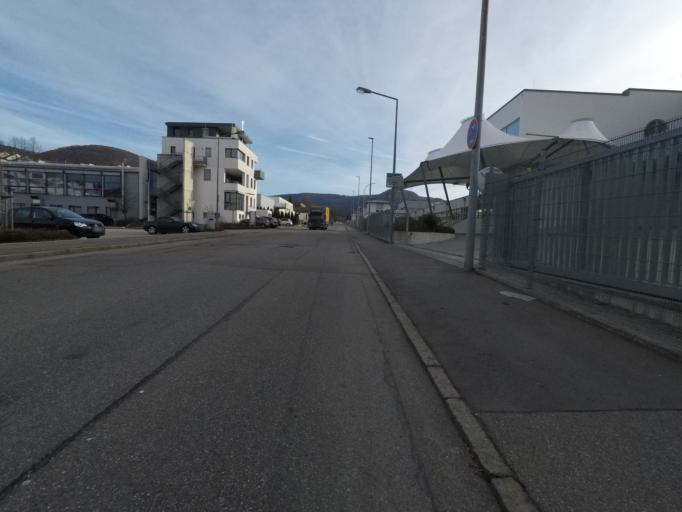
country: DE
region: Baden-Wuerttemberg
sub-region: Tuebingen Region
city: Eningen unter Achalm
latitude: 48.4771
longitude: 9.2522
